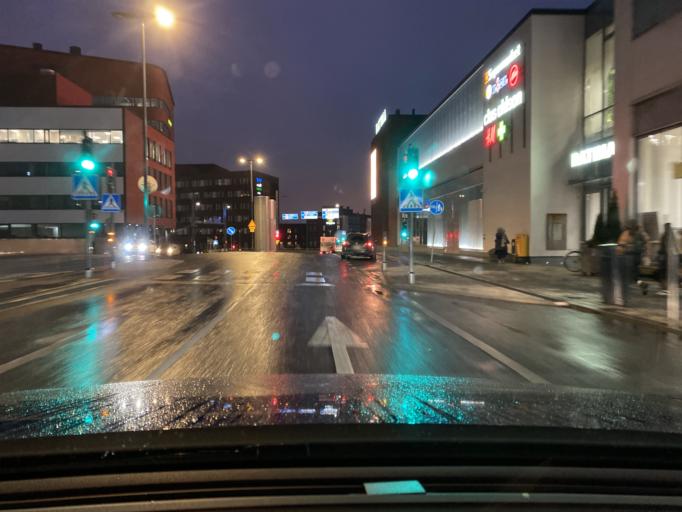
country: FI
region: Pirkanmaa
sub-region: Tampere
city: Tampere
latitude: 61.4933
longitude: 23.7686
